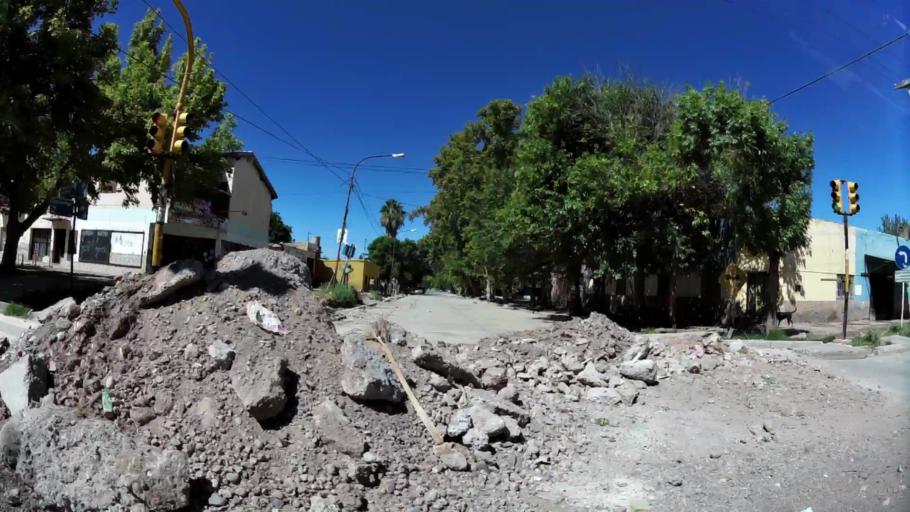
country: AR
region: Mendoza
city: Las Heras
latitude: -32.8323
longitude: -68.8333
